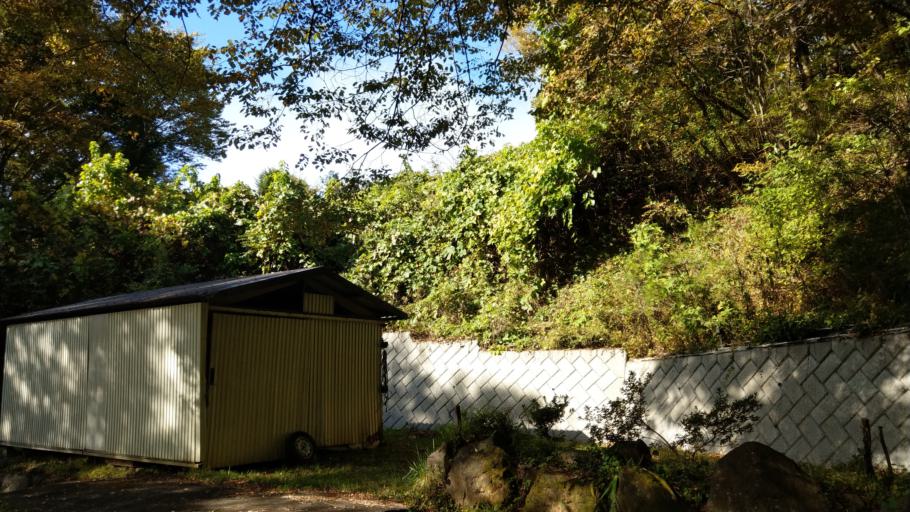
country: JP
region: Nagano
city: Komoro
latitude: 36.3556
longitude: 138.4295
